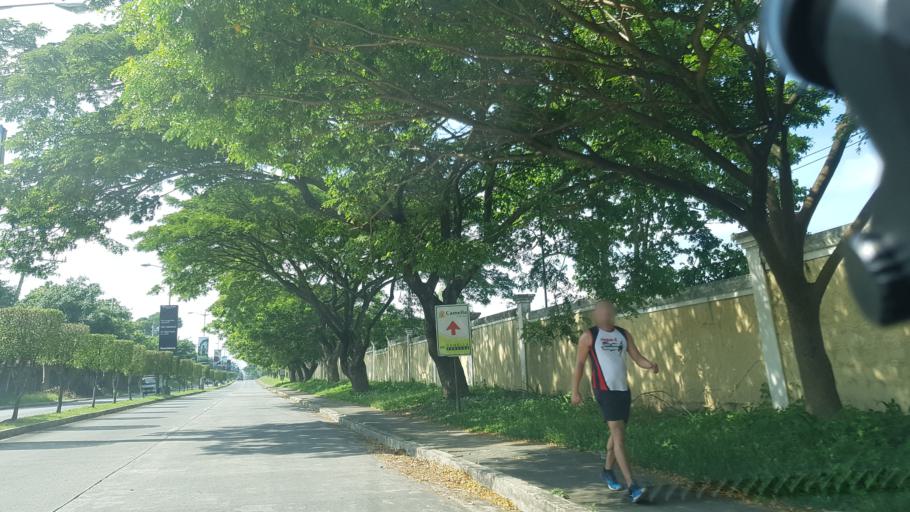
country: PH
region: Calabarzon
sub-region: Province of Laguna
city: Magsaysay
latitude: 14.3664
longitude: 121.0098
